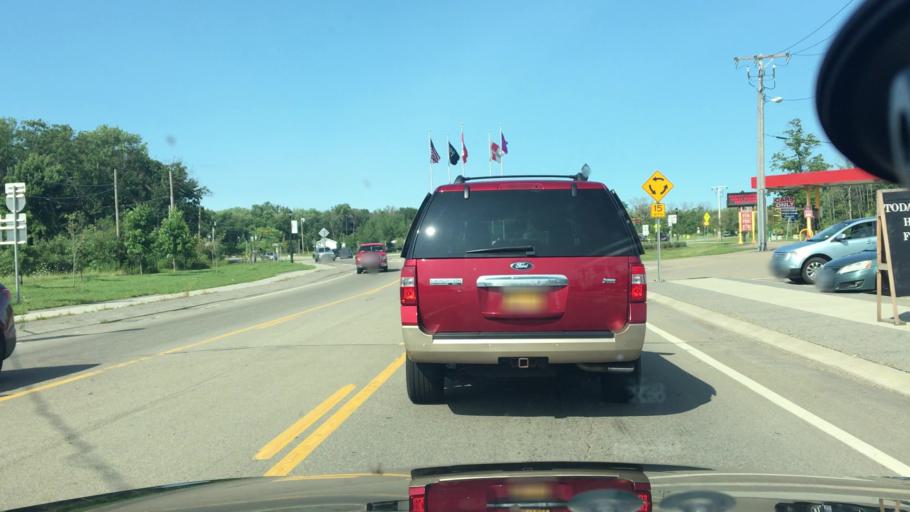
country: US
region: New York
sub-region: Erie County
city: Lake Erie Beach
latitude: 42.5691
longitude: -79.1026
